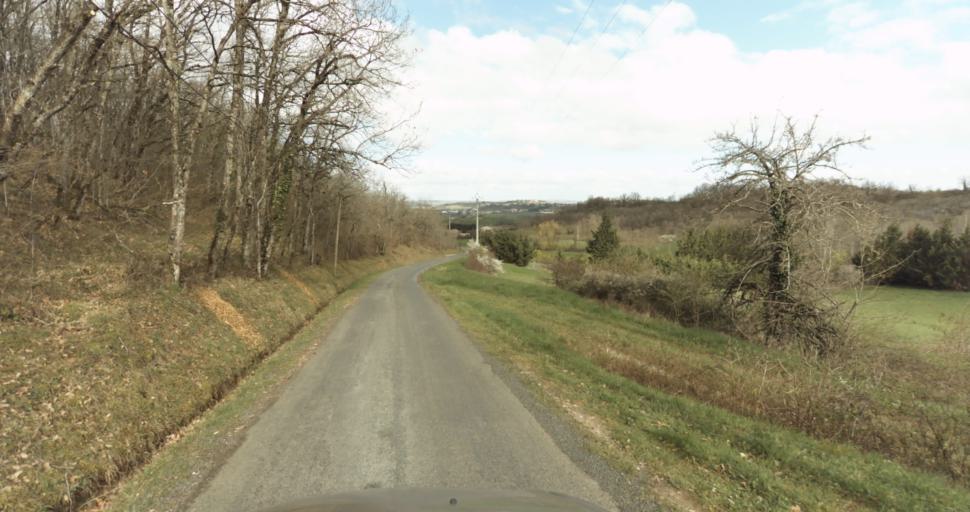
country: FR
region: Midi-Pyrenees
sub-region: Departement du Tarn
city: Puygouzon
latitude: 43.8707
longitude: 2.1880
